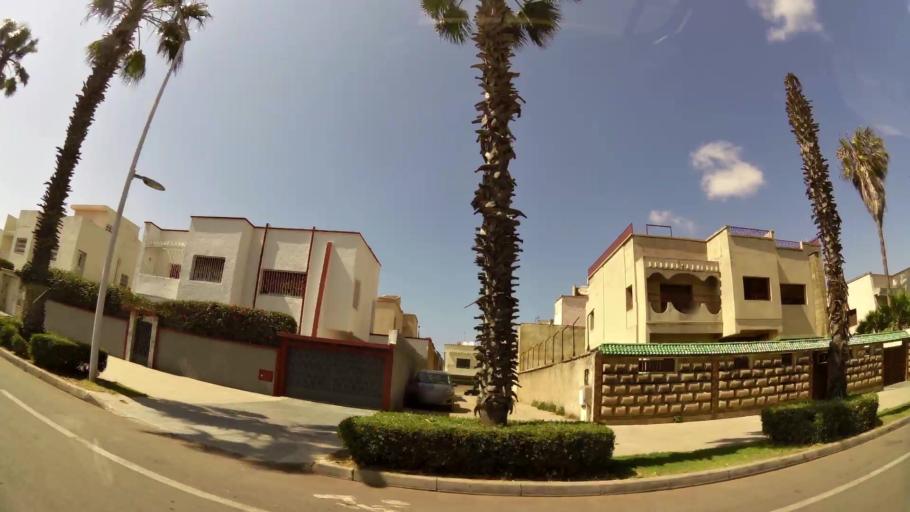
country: MA
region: Rabat-Sale-Zemmour-Zaer
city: Sale
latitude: 34.0350
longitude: -6.7924
